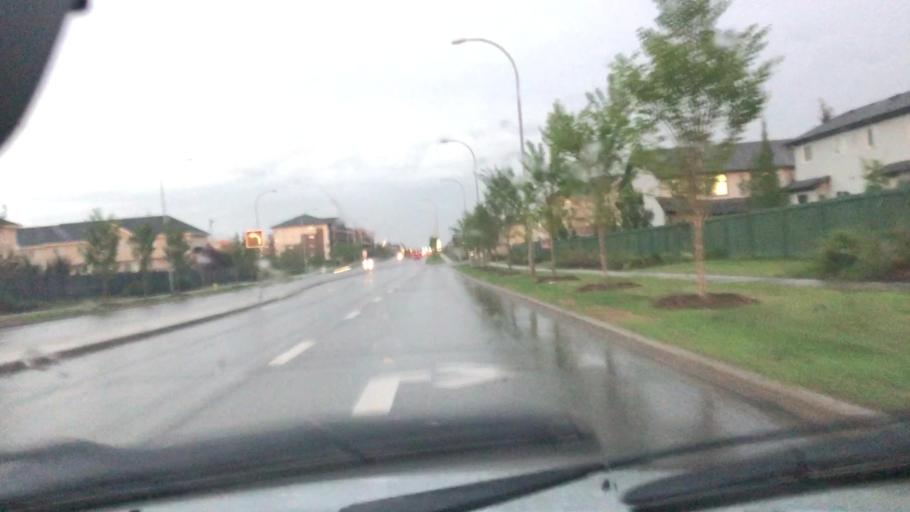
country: CA
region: Alberta
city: St. Albert
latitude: 53.6287
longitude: -113.5617
